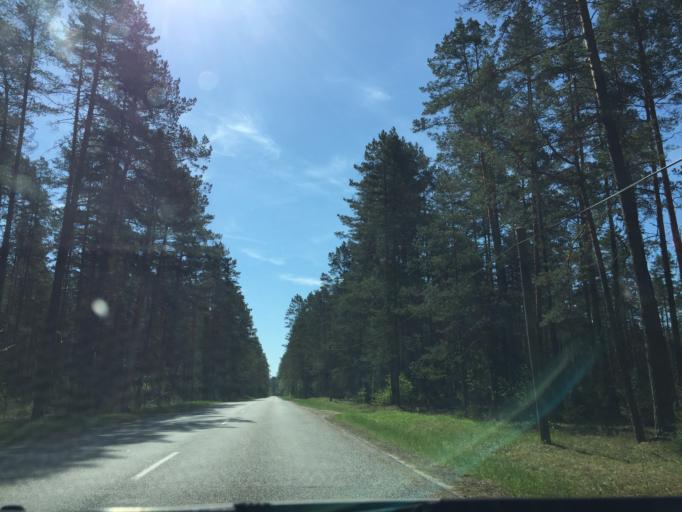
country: LV
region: Garkalne
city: Garkalne
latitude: 57.0222
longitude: 24.4354
